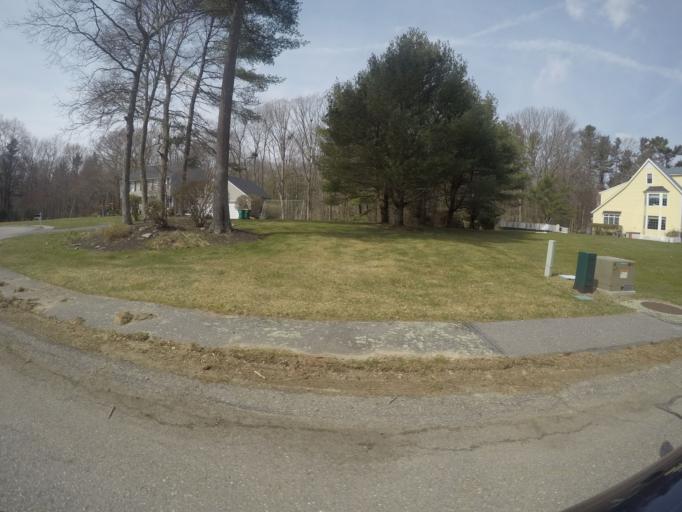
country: US
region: Massachusetts
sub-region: Bristol County
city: Easton
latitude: 42.0510
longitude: -71.1172
